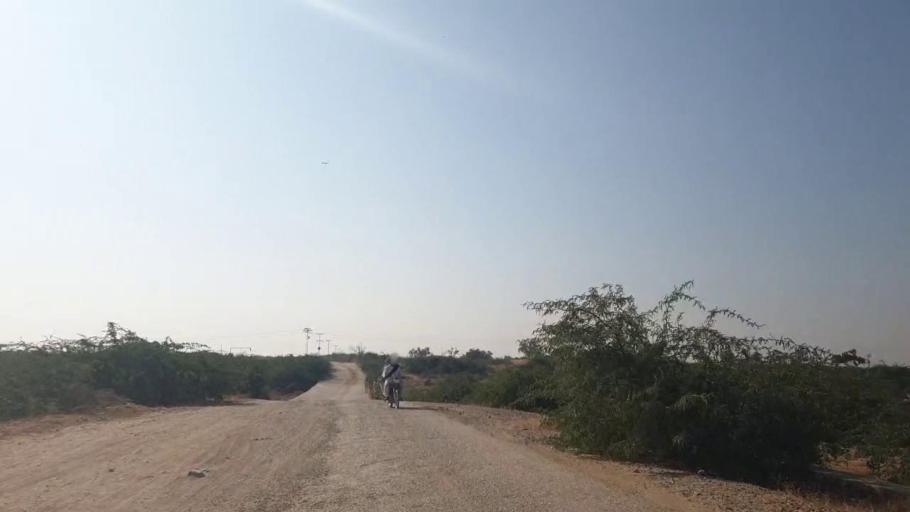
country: PK
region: Sindh
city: Thatta
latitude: 25.1394
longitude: 67.7719
